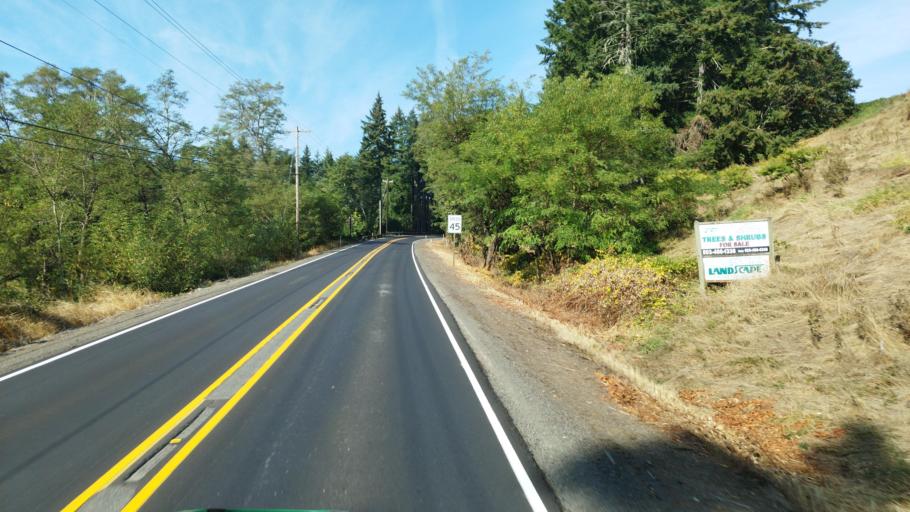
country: US
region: Oregon
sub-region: Washington County
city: Bethany
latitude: 45.5957
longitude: -122.8671
